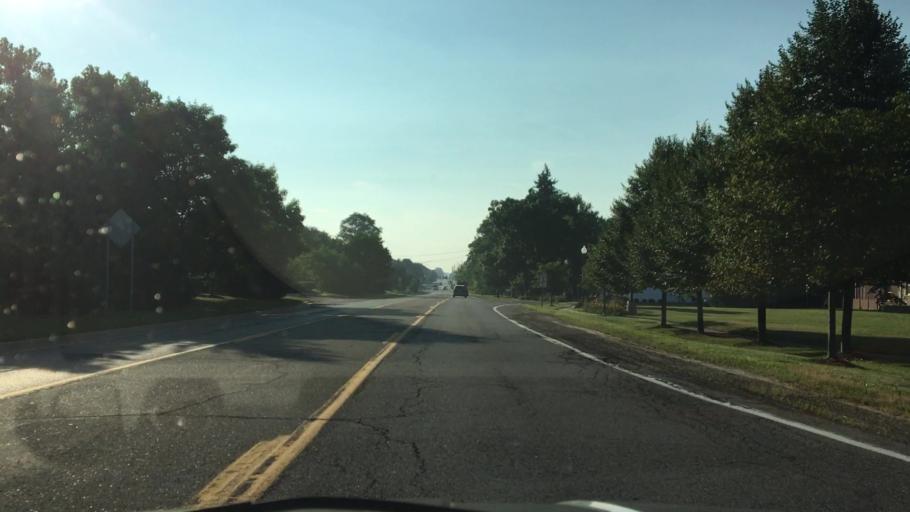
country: US
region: Michigan
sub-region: Oakland County
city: South Lyon
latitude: 42.5126
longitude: -83.6203
